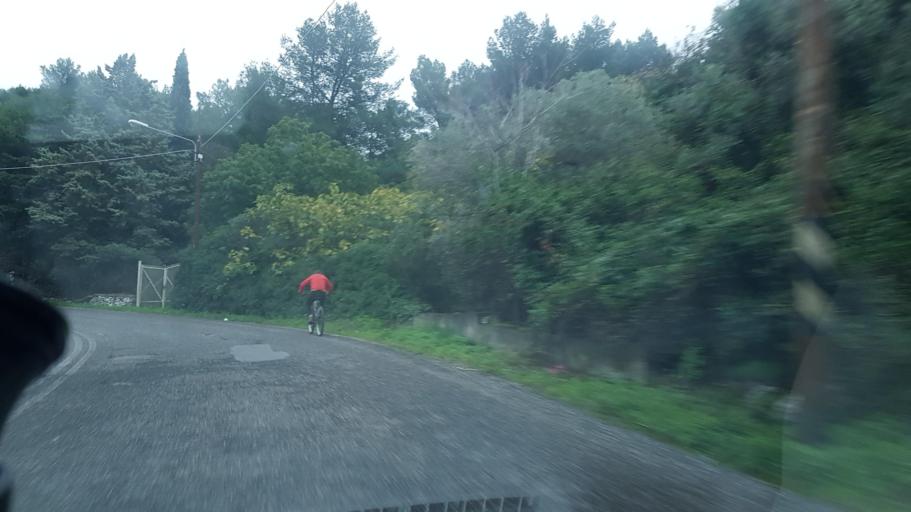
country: IT
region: Apulia
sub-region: Provincia di Brindisi
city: Ostuni
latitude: 40.7299
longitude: 17.5714
